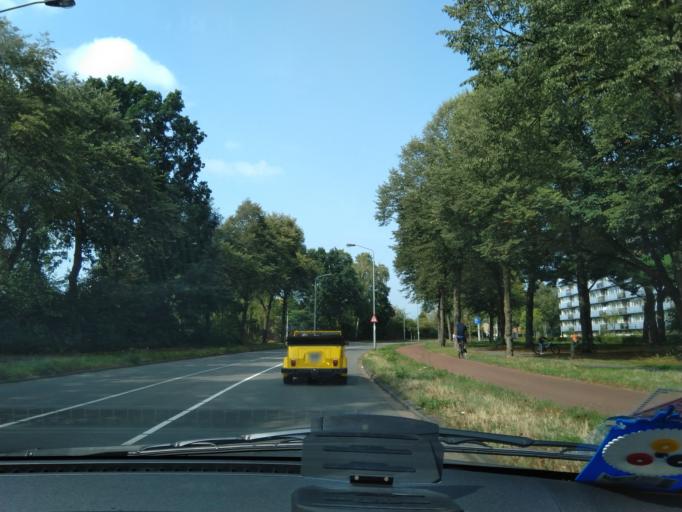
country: NL
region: North Brabant
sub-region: Gemeente Breda
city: Hoge Vucht
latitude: 51.5905
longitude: 4.8204
